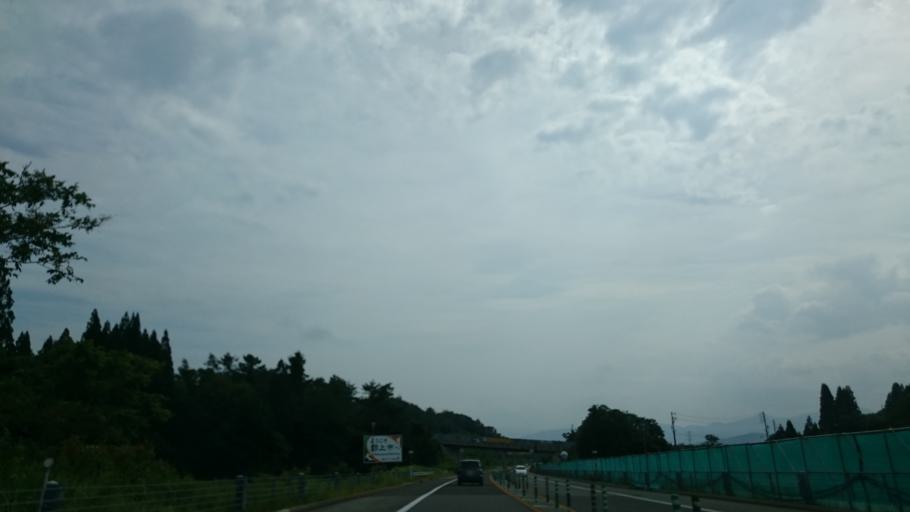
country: JP
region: Gifu
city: Gujo
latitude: 35.9989
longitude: 136.9254
